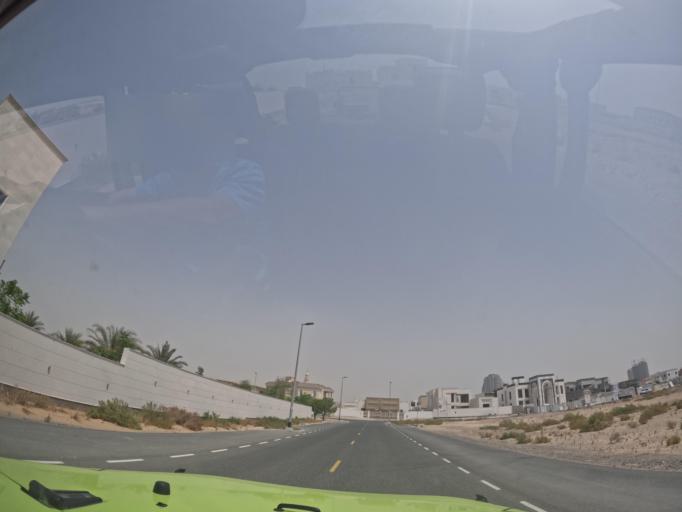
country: AE
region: Dubai
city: Dubai
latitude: 25.1299
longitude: 55.3697
